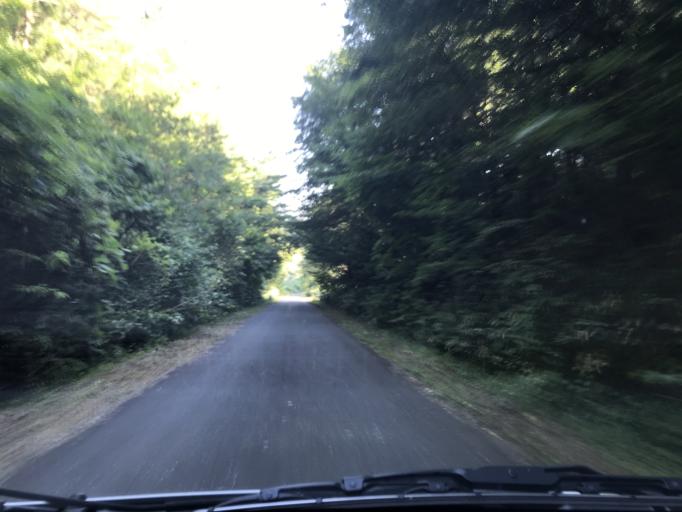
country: JP
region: Iwate
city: Mizusawa
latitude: 39.0628
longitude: 141.0409
